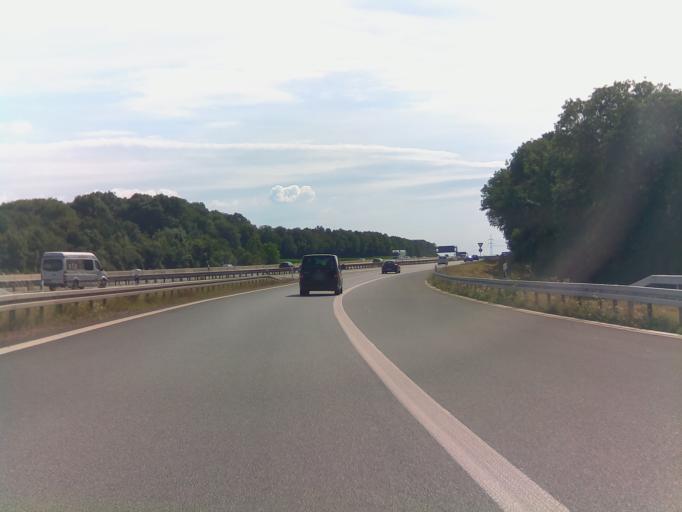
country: DE
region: Bavaria
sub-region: Regierungsbezirk Unterfranken
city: Biebelried
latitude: 49.7777
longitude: 10.0862
